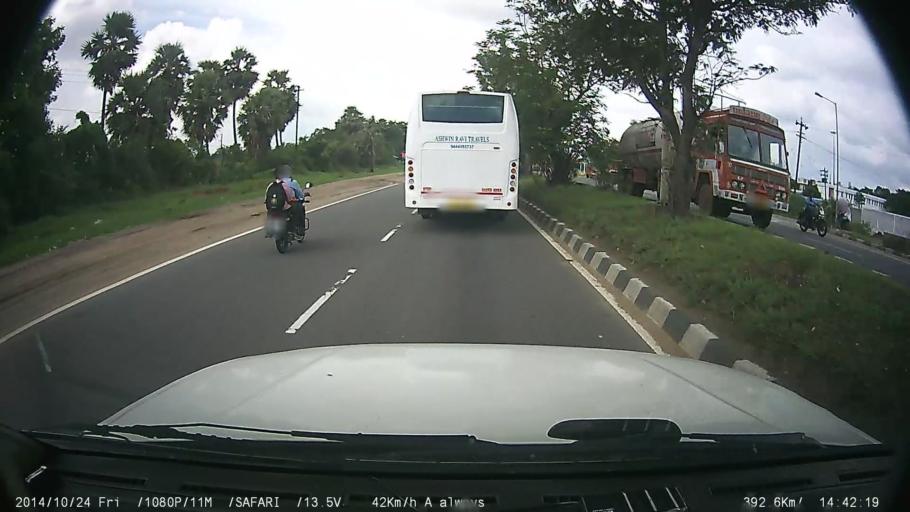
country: IN
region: Tamil Nadu
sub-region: Kancheepuram
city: Singapperumalkovil
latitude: 12.7681
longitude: 80.0063
